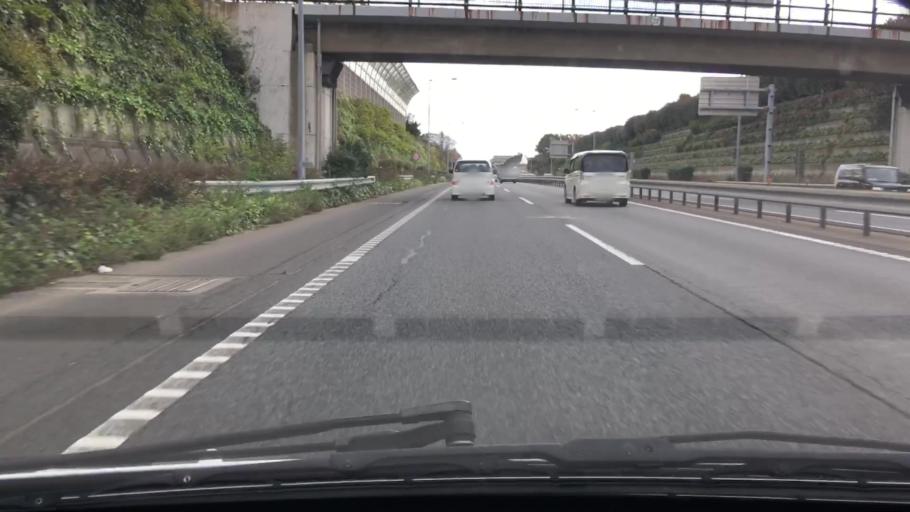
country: JP
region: Chiba
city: Chiba
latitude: 35.6671
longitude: 140.0733
